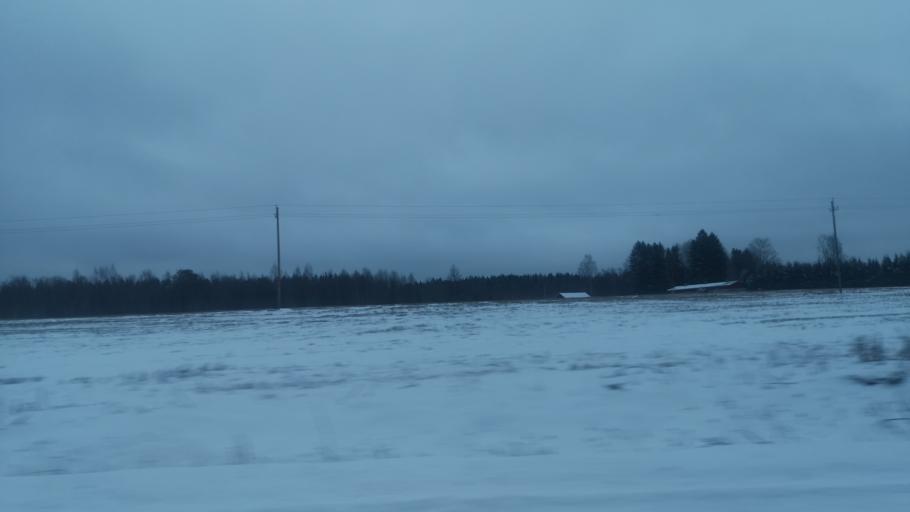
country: FI
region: Southern Savonia
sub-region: Savonlinna
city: Savonlinna
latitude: 62.0011
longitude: 28.7437
